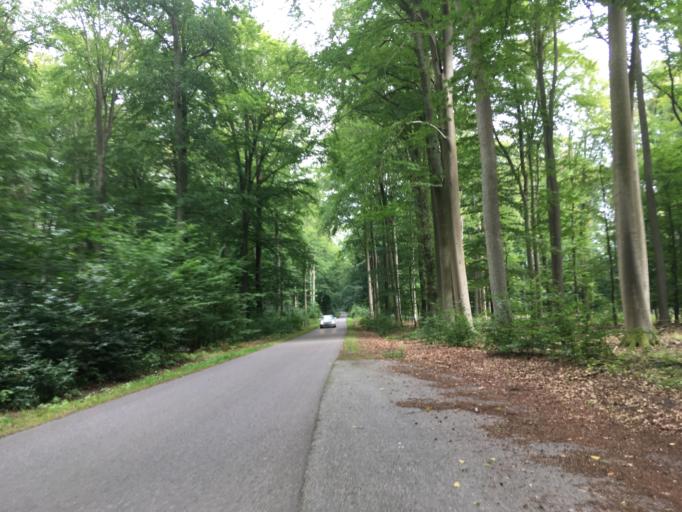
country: DE
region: Brandenburg
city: Althuttendorf
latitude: 53.0192
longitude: 13.8001
